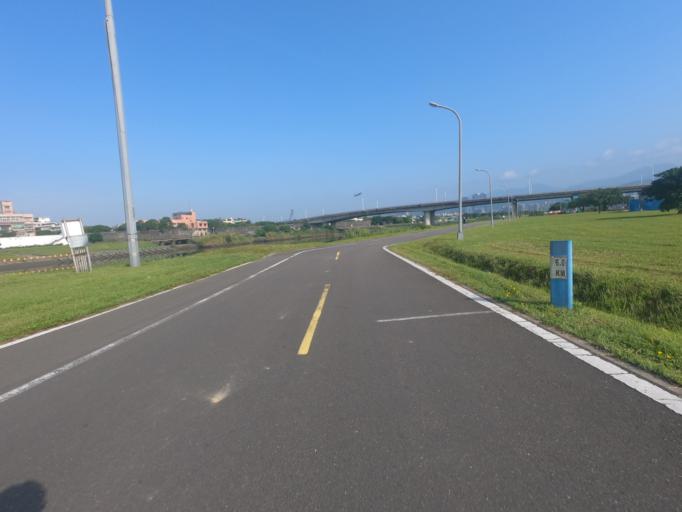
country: TW
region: Taipei
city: Taipei
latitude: 25.0618
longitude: 121.5712
